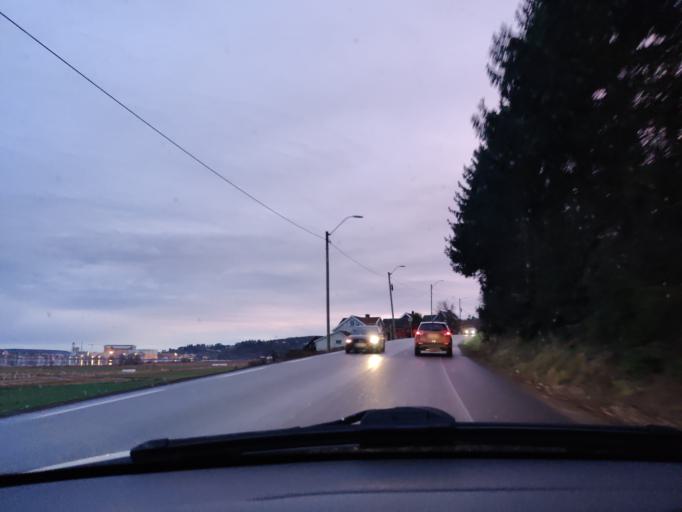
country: NO
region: Vestfold
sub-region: Tonsberg
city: Sem
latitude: 59.2748
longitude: 10.3649
